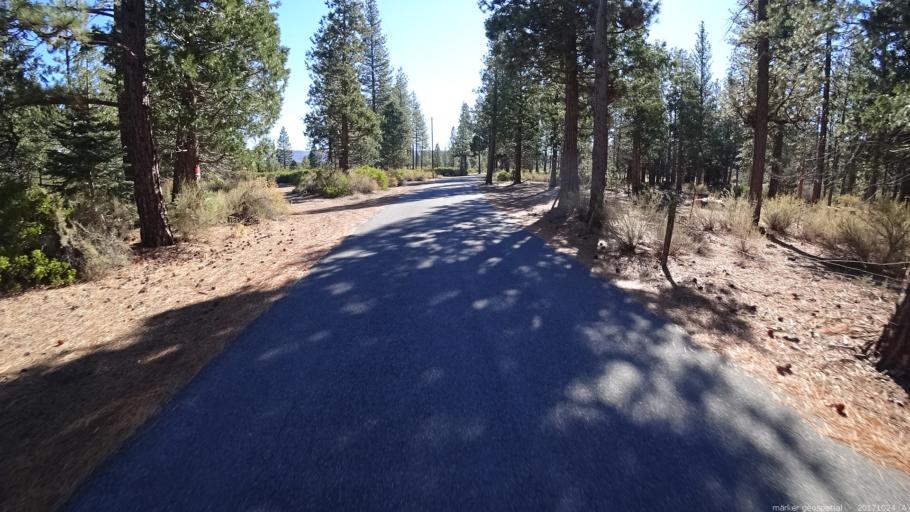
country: US
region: California
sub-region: Shasta County
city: Burney
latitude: 40.7538
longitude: -121.4804
